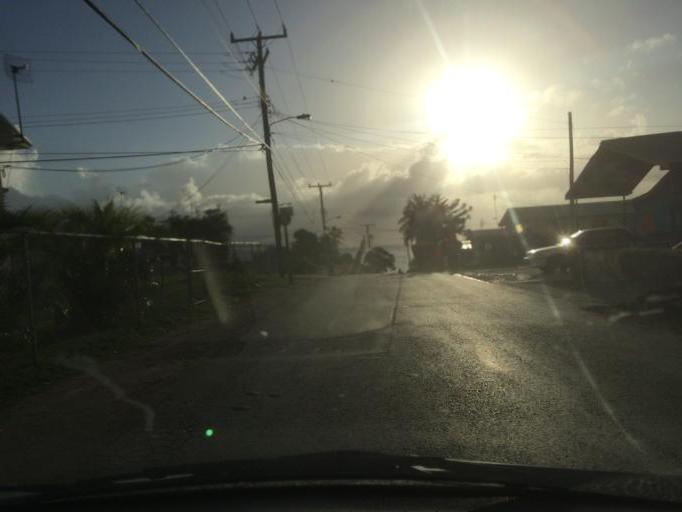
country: BB
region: Saint Lucy
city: Checker Hall
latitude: 13.2814
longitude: -59.6458
